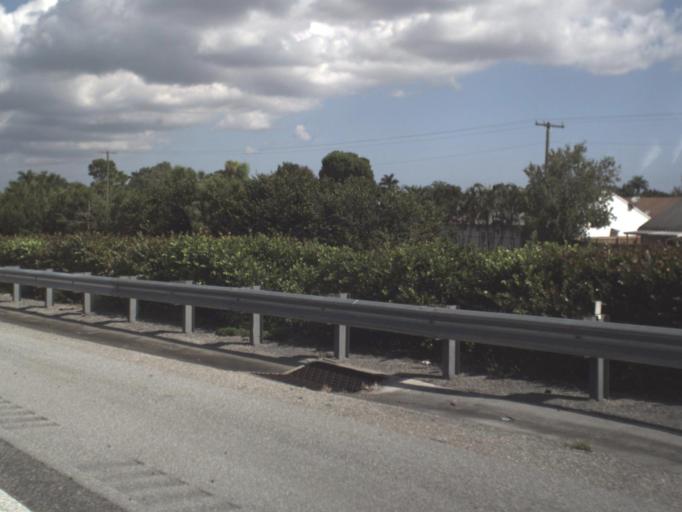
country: US
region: Florida
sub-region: Palm Beach County
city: Greenacres City
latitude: 26.5940
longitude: -80.1733
